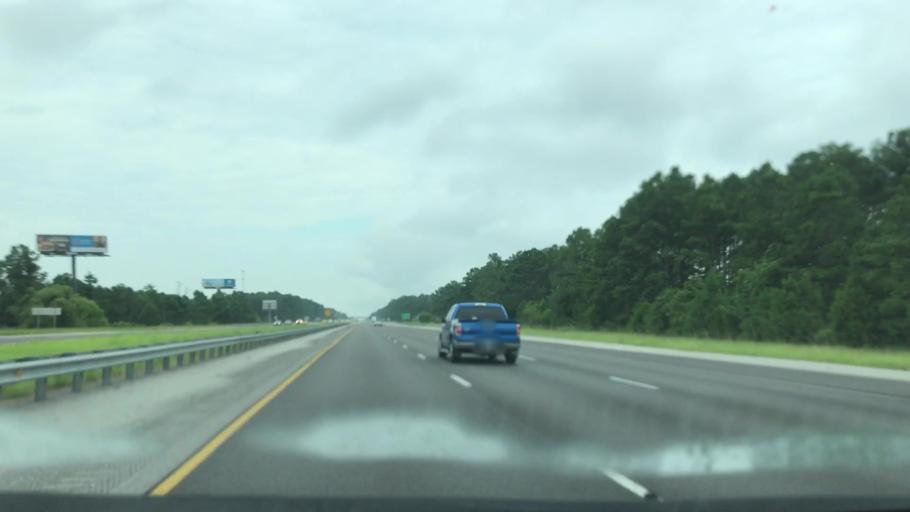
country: US
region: Georgia
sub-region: Liberty County
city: Midway
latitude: 31.6487
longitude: -81.3988
